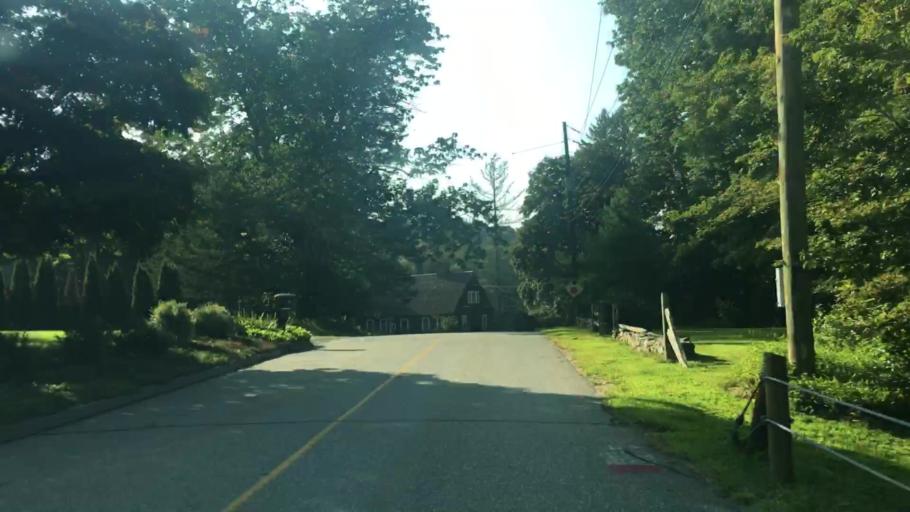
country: US
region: Connecticut
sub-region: Middlesex County
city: Chester Center
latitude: 41.3987
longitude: -72.4571
